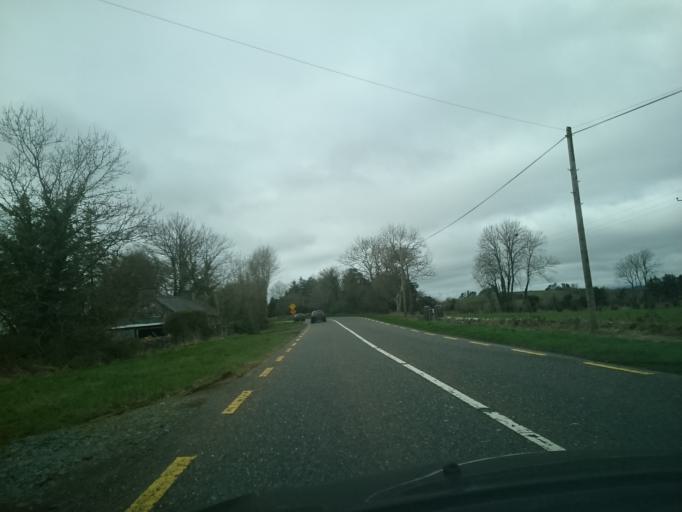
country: IE
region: Connaught
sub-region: Maigh Eo
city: Castlebar
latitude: 53.8203
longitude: -9.3779
